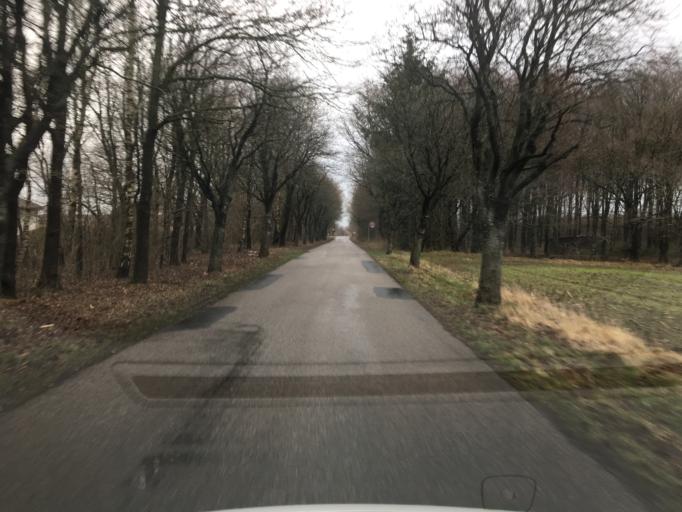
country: DK
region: South Denmark
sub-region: Aabenraa Kommune
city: Tinglev
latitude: 54.9261
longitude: 9.2320
